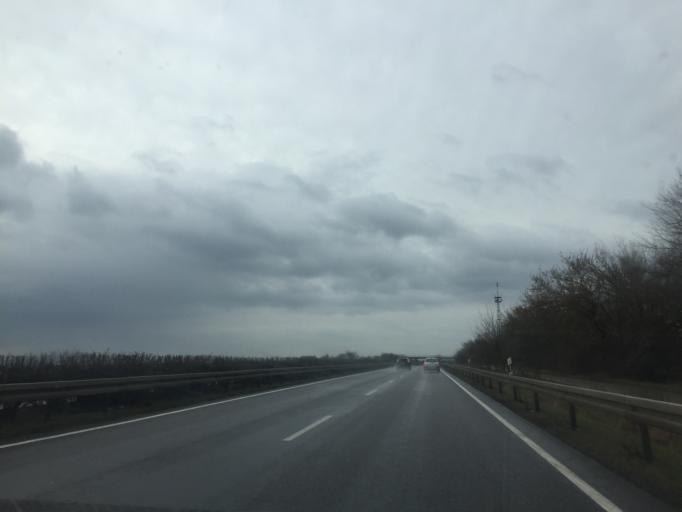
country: DE
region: Saxony-Anhalt
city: Hohendodeleben
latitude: 52.0607
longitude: 11.5452
